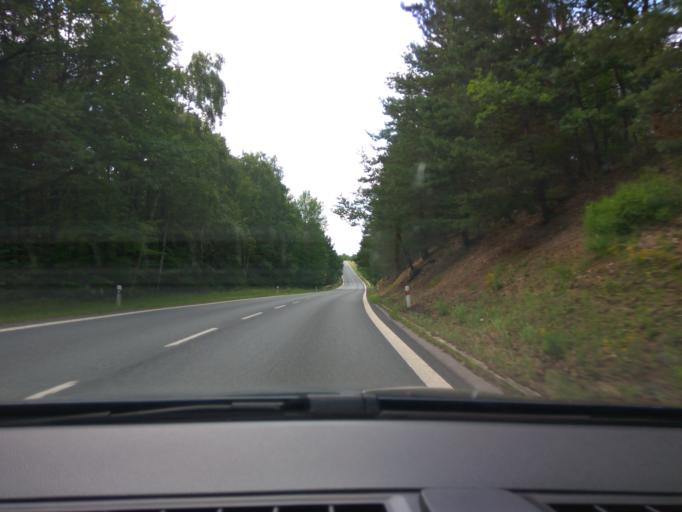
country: CZ
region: Jihocesky
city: Milevsko
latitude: 49.4648
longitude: 14.3151
